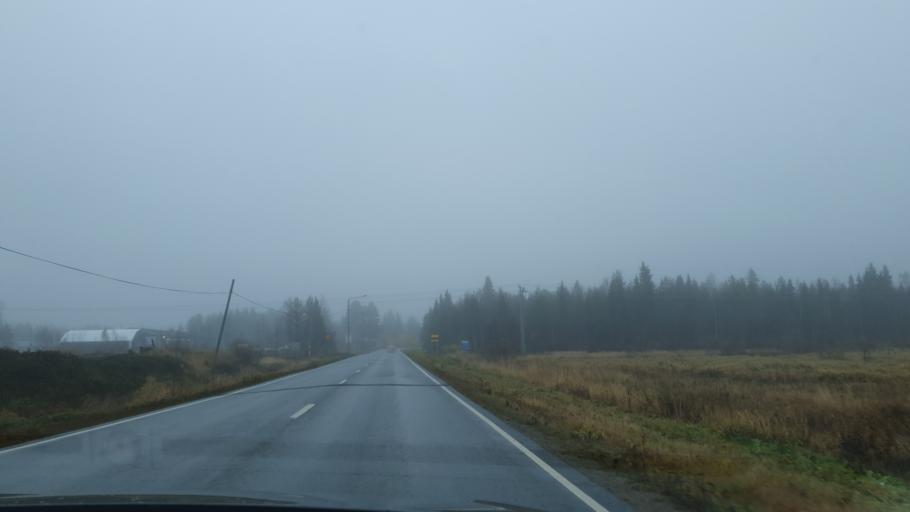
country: FI
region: Lapland
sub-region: Tunturi-Lappi
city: Kittilae
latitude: 67.6693
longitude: 24.8680
